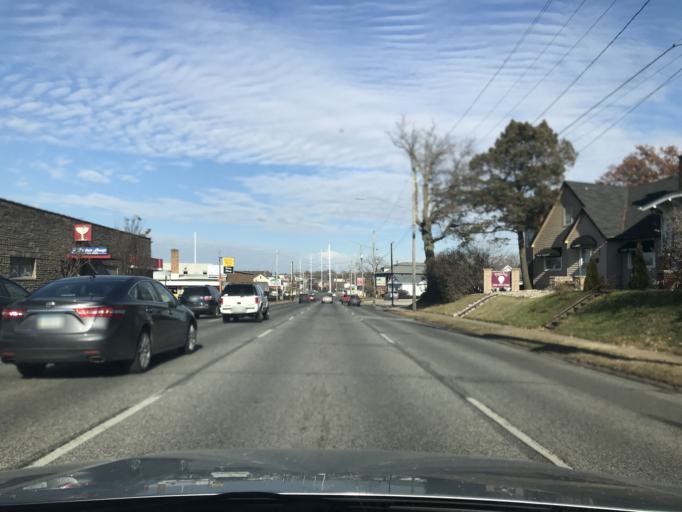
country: US
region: Iowa
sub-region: Scott County
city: Davenport
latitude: 41.5504
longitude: -90.5704
